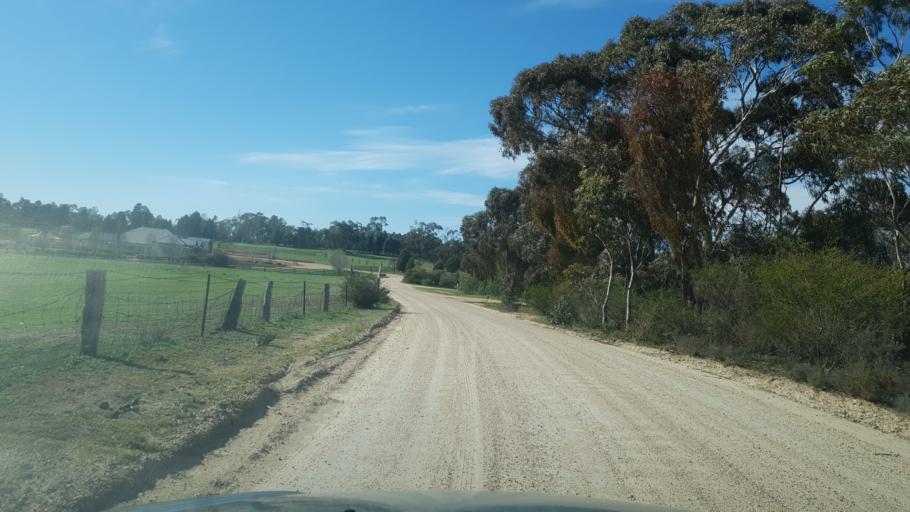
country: AU
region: South Australia
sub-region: Barossa
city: Williamstown
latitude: -34.6562
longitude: 138.8254
